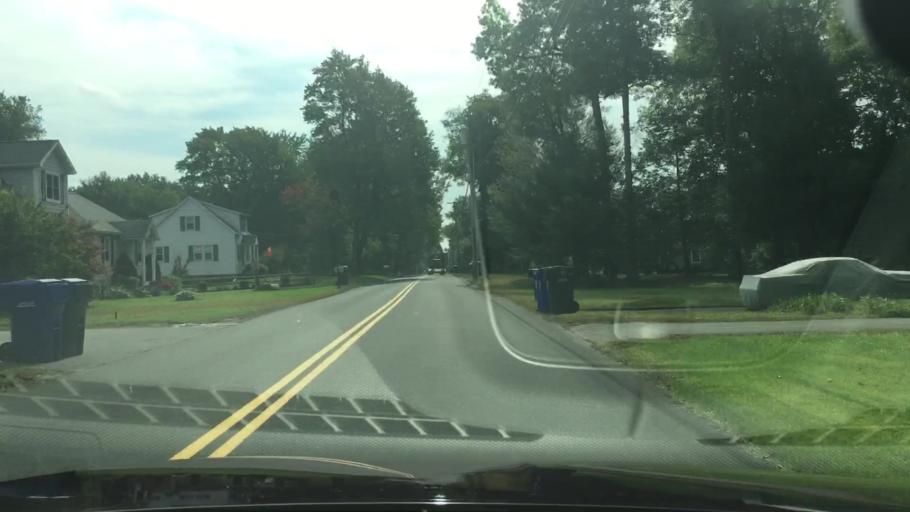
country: US
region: Connecticut
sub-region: Tolland County
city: Ellington
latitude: 41.9419
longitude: -72.4800
